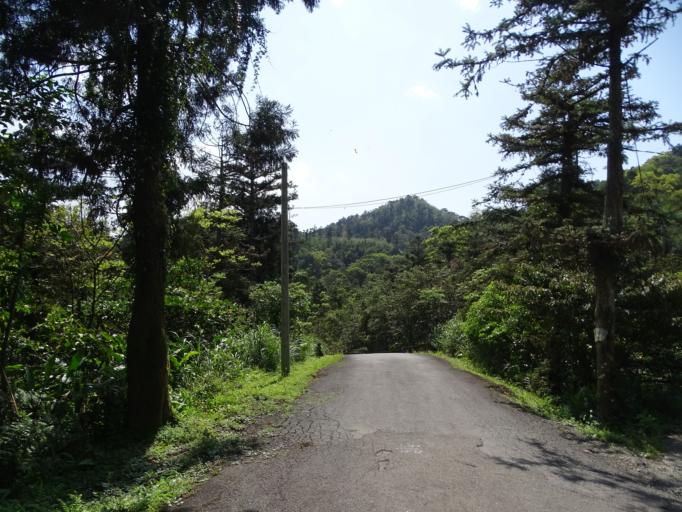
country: TW
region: Taiwan
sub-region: Keelung
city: Keelung
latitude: 25.0447
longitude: 121.7563
